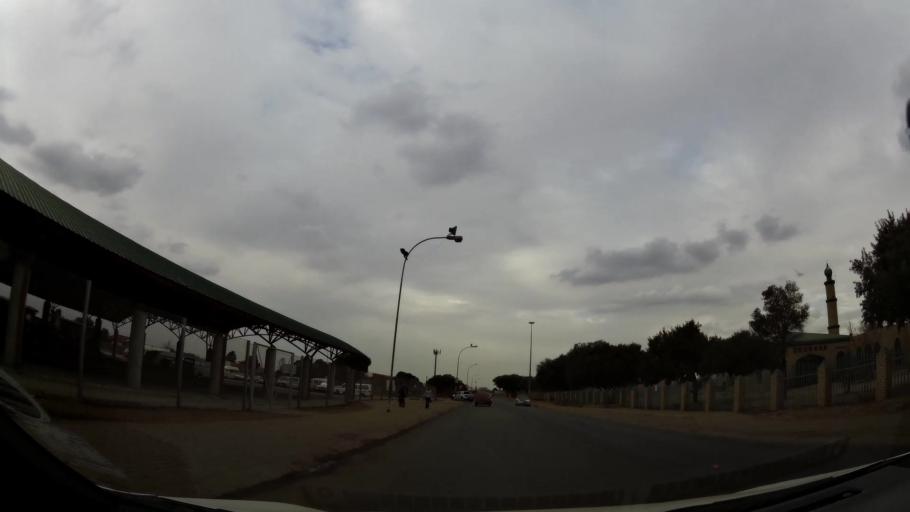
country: ZA
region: Gauteng
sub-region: Ekurhuleni Metropolitan Municipality
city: Germiston
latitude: -26.3891
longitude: 28.1434
